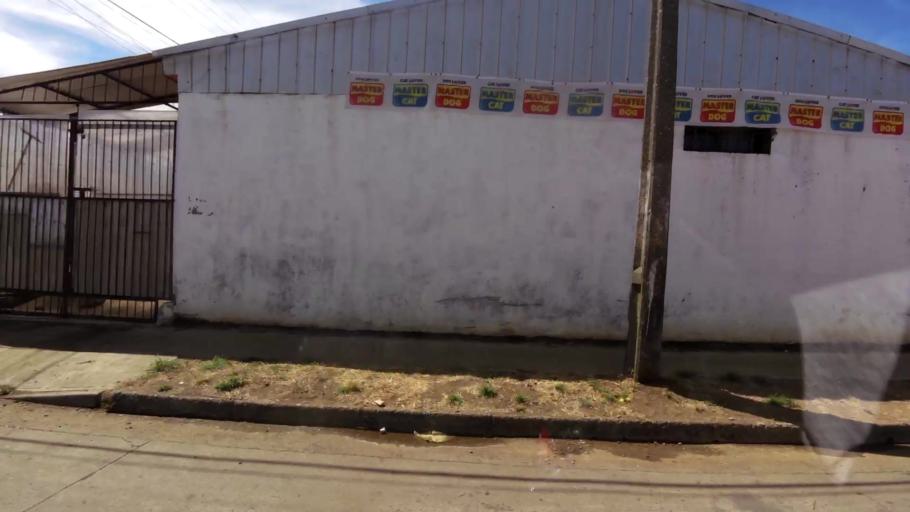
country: CL
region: Biobio
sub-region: Provincia de Concepcion
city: Talcahuano
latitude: -36.7127
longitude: -73.1368
